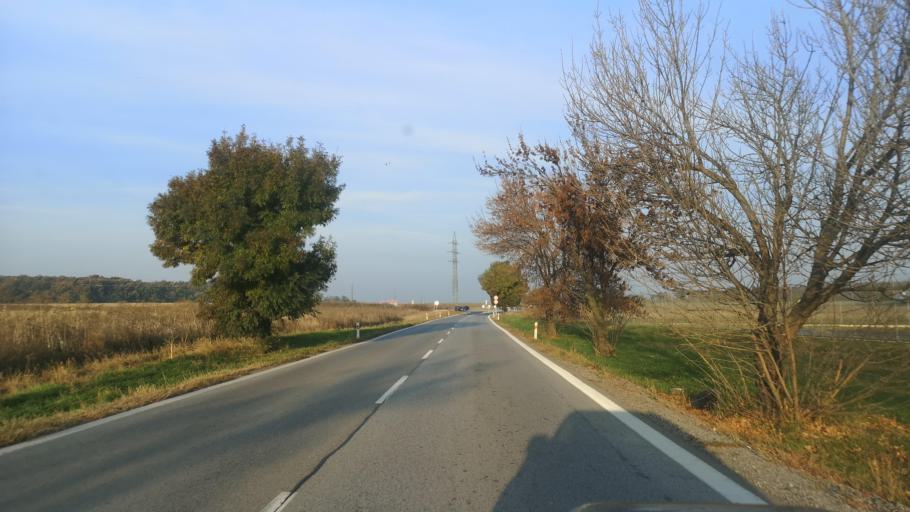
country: SK
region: Bratislavsky
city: Senec
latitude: 48.2465
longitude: 17.3471
